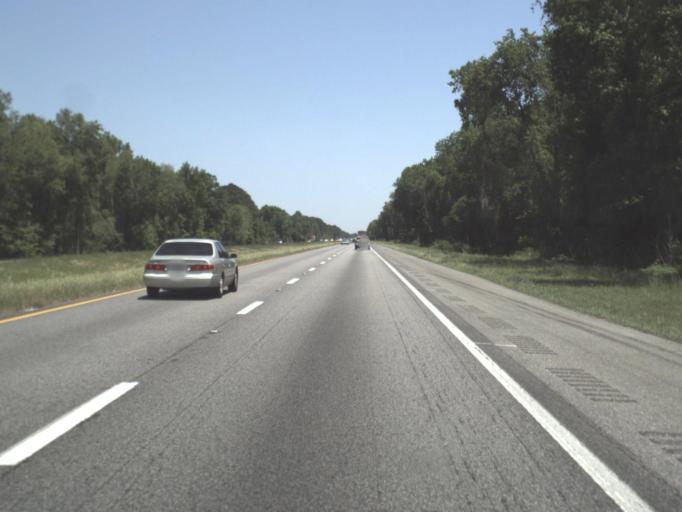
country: US
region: Florida
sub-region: Jefferson County
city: Monticello
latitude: 30.4676
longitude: -83.8055
